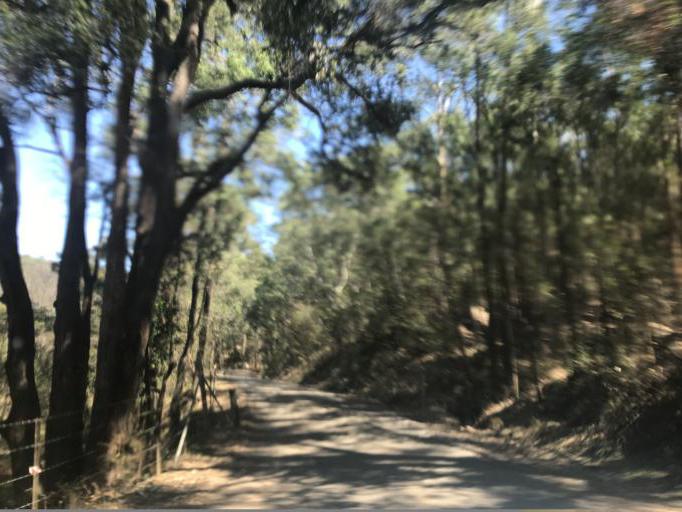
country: AU
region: New South Wales
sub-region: Wyong Shire
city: Little Jilliby
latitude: -33.2003
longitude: 150.9971
